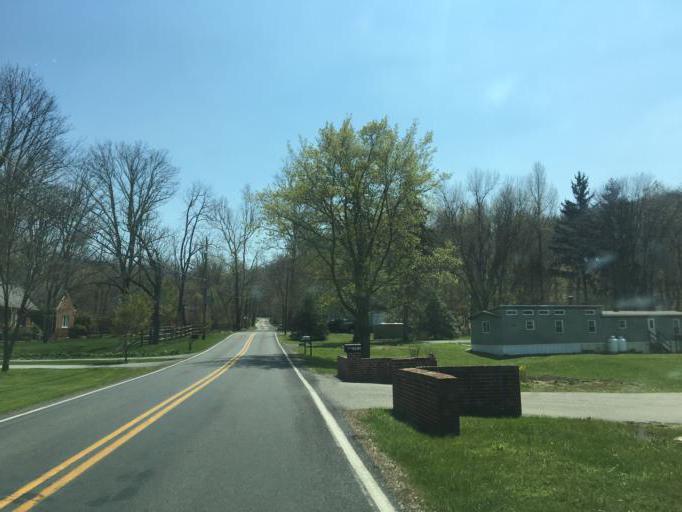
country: US
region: Maryland
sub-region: Washington County
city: Smithsburg
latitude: 39.6460
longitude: -77.5668
